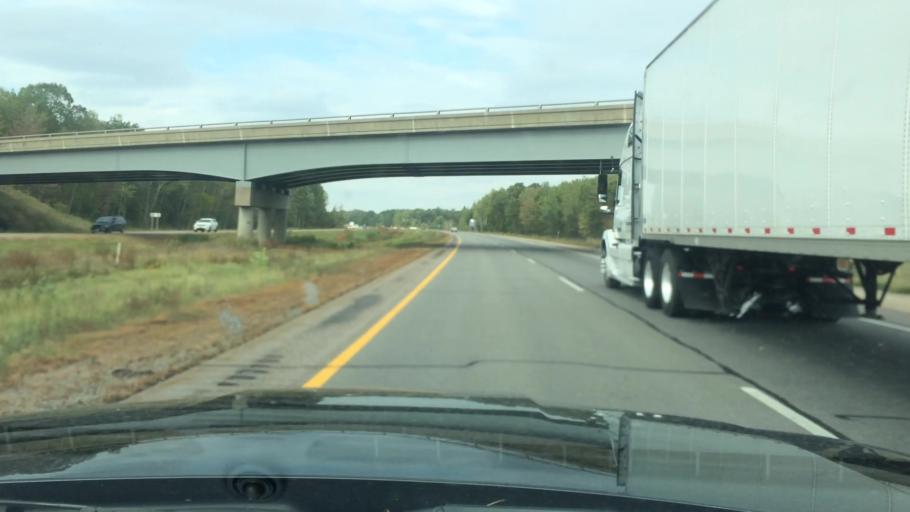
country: US
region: Wisconsin
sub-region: Marathon County
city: Mosinee
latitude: 44.7134
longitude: -89.6596
